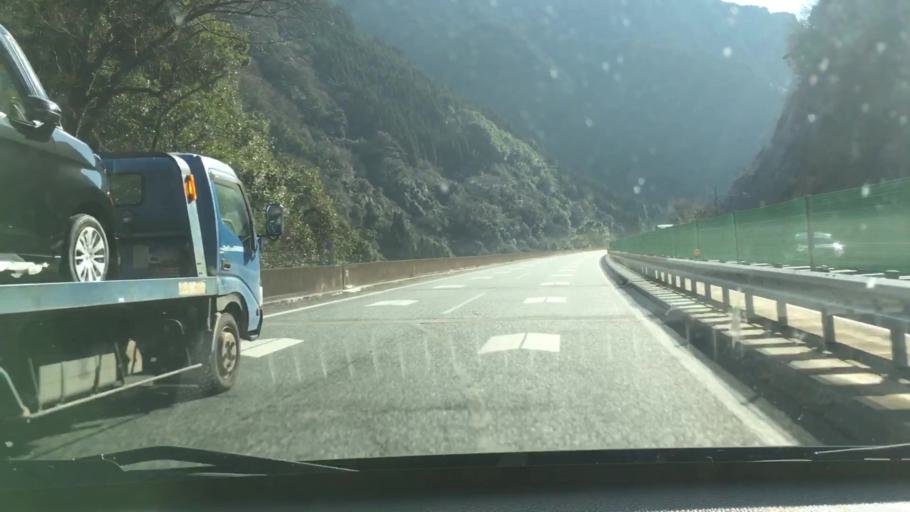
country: JP
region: Kumamoto
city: Hitoyoshi
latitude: 32.3228
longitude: 130.7581
